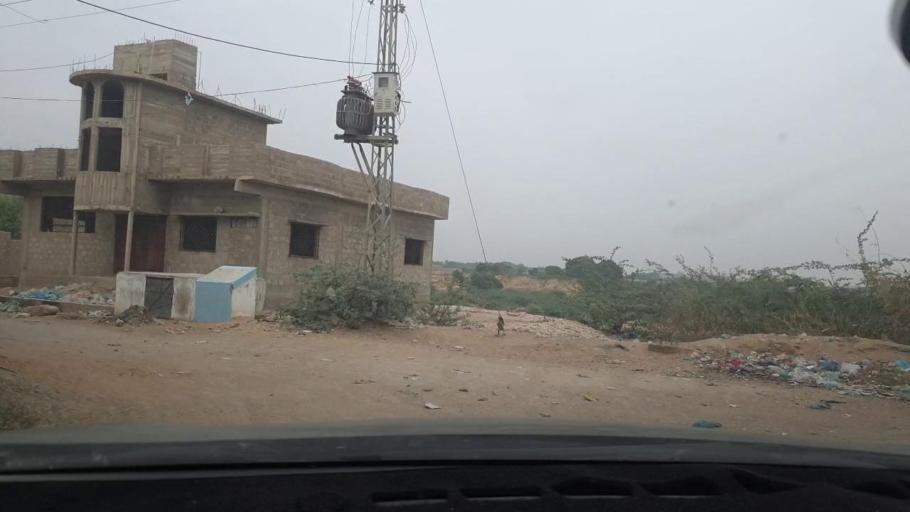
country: PK
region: Sindh
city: Malir Cantonment
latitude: 24.8692
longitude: 67.2525
